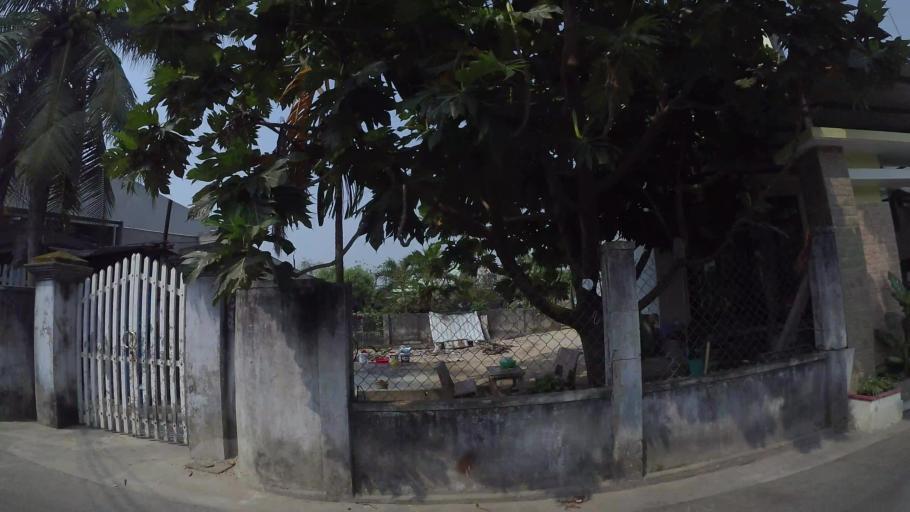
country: VN
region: Da Nang
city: Ngu Hanh Son
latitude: 15.9884
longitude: 108.2408
